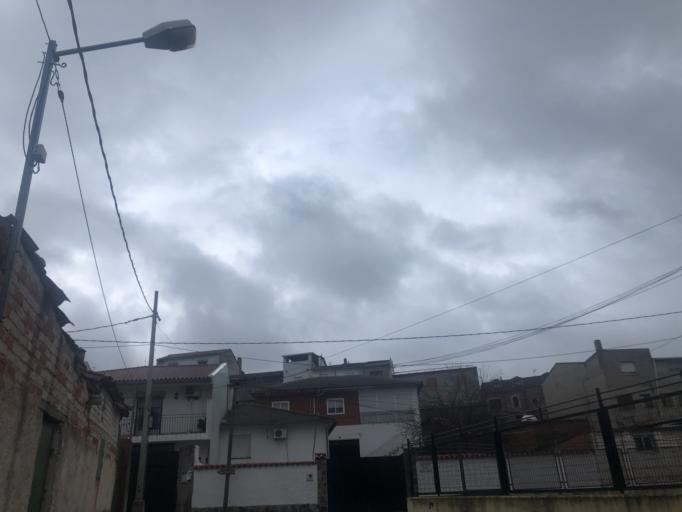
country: ES
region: Castille-La Mancha
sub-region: Provincia de Ciudad Real
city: Navalpino
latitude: 39.3292
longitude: -4.6511
